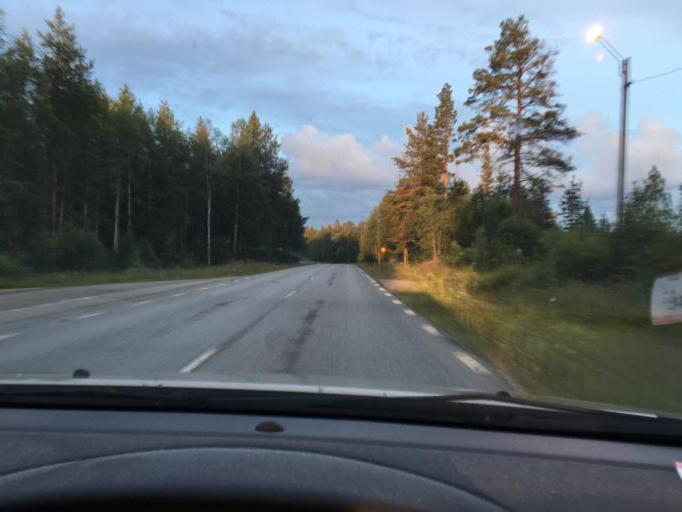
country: SE
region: Norrbotten
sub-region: Lulea Kommun
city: Ranea
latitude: 66.0443
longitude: 22.2892
